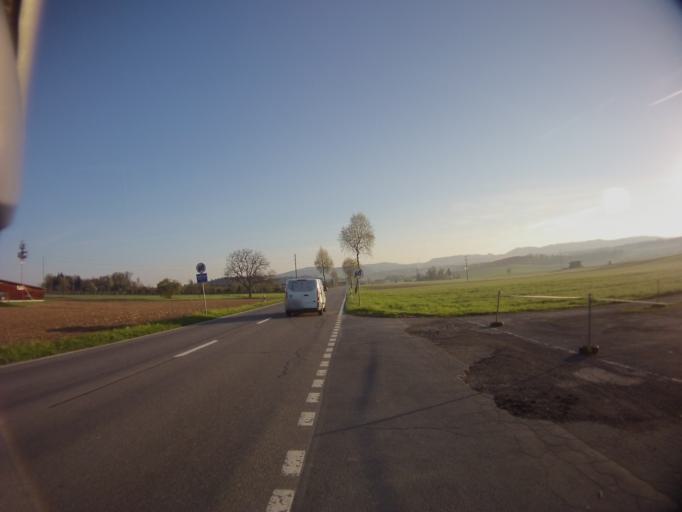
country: CH
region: Zug
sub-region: Zug
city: Cham
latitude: 47.2012
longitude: 8.4540
